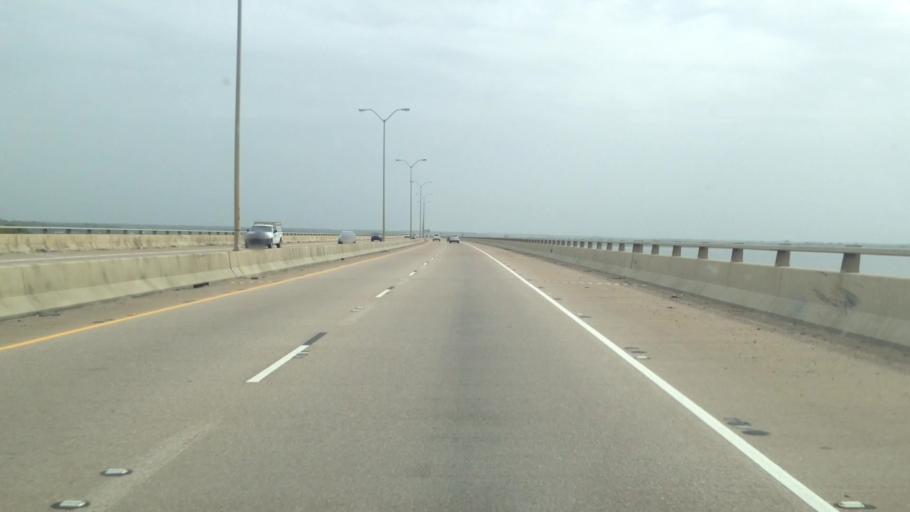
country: US
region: Louisiana
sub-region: Caddo Parish
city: Shreveport
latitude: 32.4968
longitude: -93.8204
